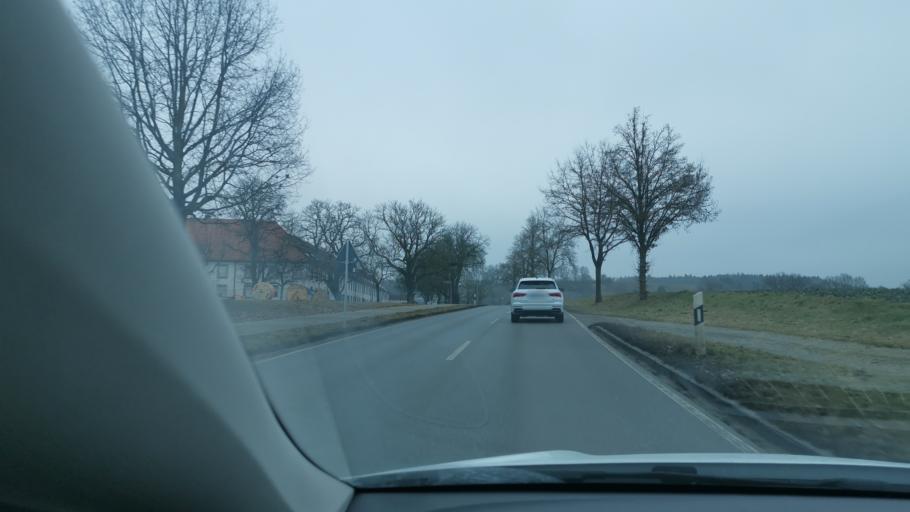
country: DE
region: Bavaria
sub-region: Swabia
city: Thierhaupten
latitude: 48.5594
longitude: 10.9113
